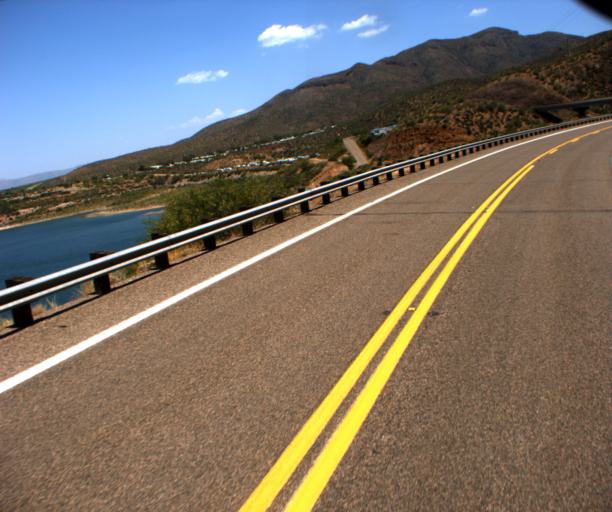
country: US
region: Arizona
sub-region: Gila County
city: Tonto Basin
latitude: 33.6730
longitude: -111.1439
